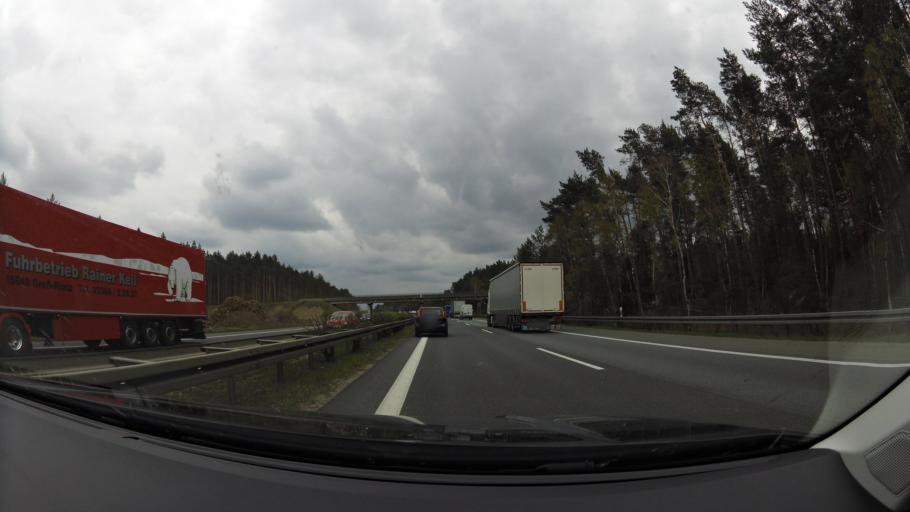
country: DE
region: Brandenburg
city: Glienicke
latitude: 52.6841
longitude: 13.3398
